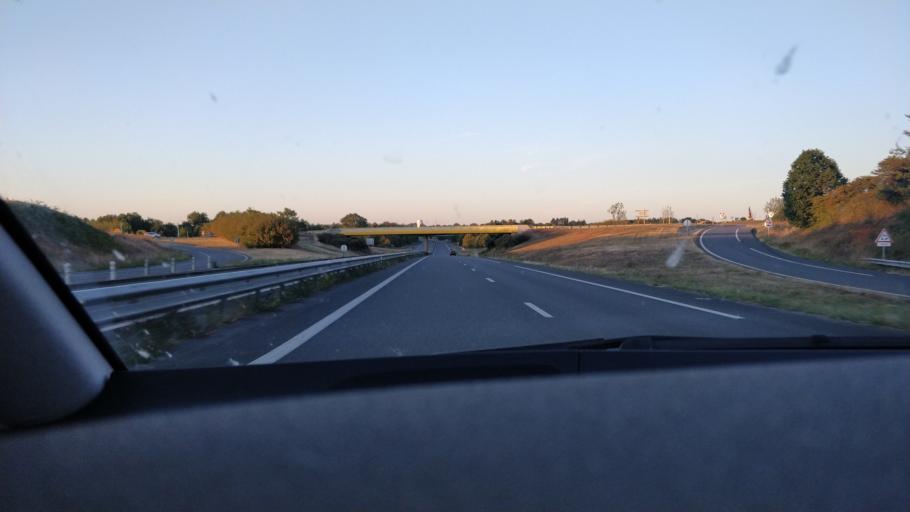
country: FR
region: Poitou-Charentes
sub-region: Departement de la Charente
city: Chasseneuil-sur-Bonnieure
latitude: 45.8111
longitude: 0.4490
